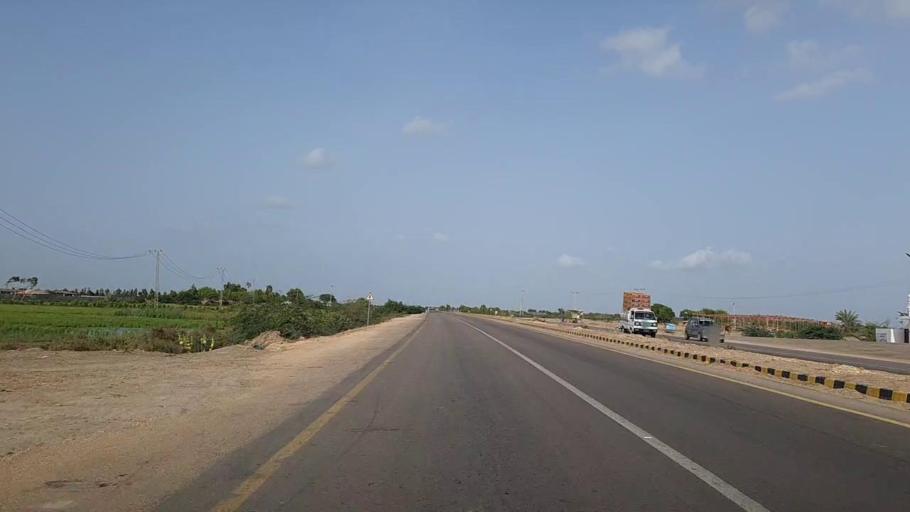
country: PK
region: Sindh
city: Thatta
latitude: 24.7429
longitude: 67.7803
